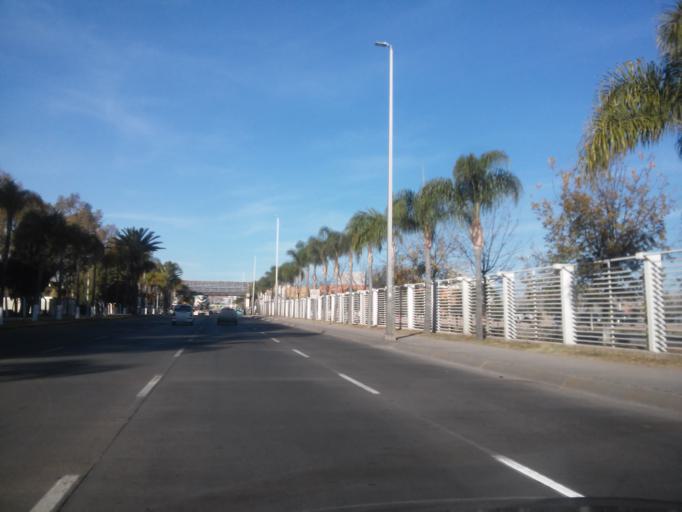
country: MX
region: Durango
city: Victoria de Durango
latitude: 24.0340
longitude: -104.6456
